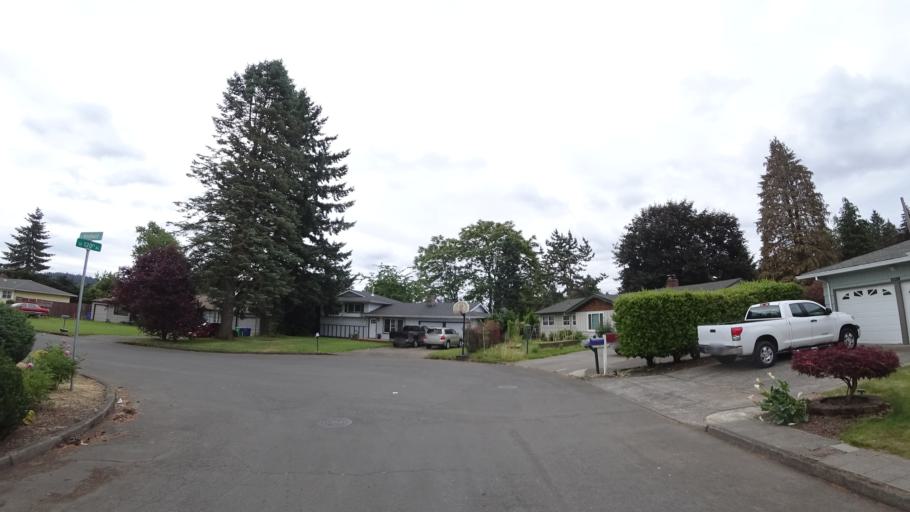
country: US
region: Oregon
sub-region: Multnomah County
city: Lents
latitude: 45.5010
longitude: -122.5398
